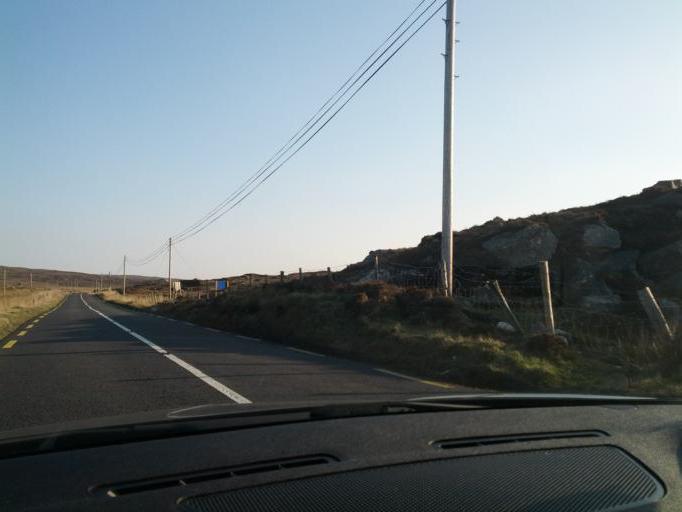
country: IE
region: Connaught
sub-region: County Galway
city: Oughterard
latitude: 53.3572
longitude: -9.5424
